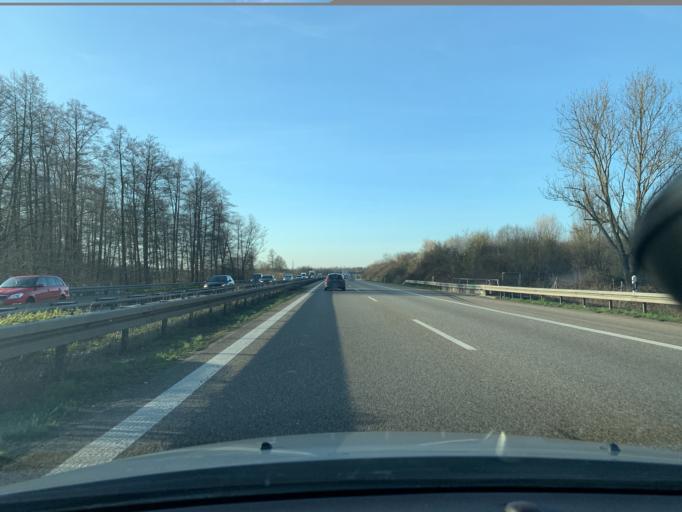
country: DE
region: Baden-Wuerttemberg
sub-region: Freiburg Region
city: Teningen
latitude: 48.0823
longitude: 7.8021
